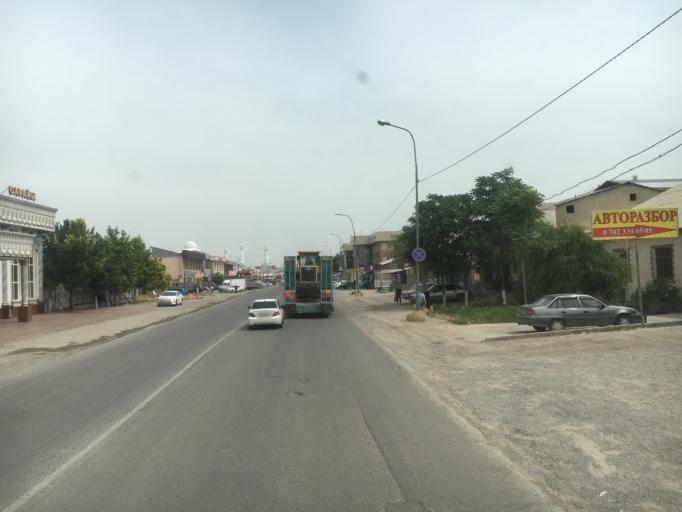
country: KZ
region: Ongtustik Qazaqstan
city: Shymkent
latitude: 42.3470
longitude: 69.5270
